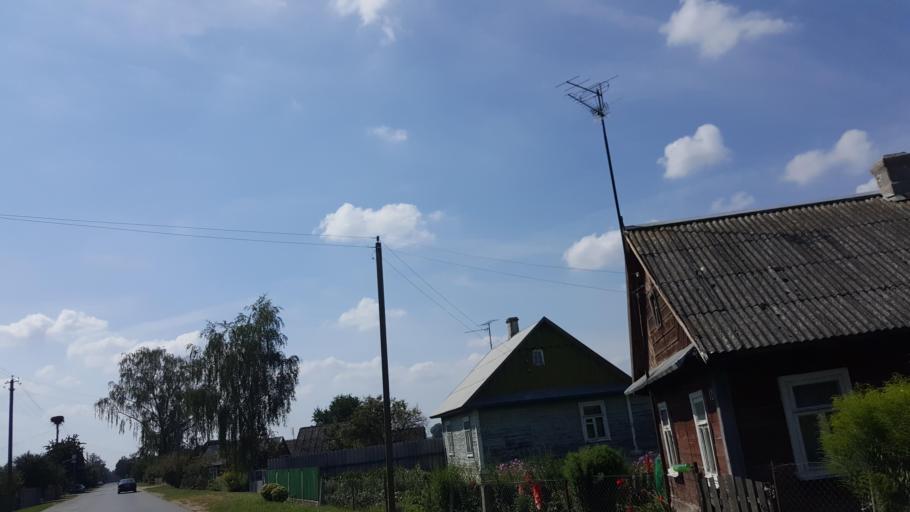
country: PL
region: Podlasie
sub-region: Powiat hajnowski
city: Czeremcha
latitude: 52.5013
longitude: 23.5733
